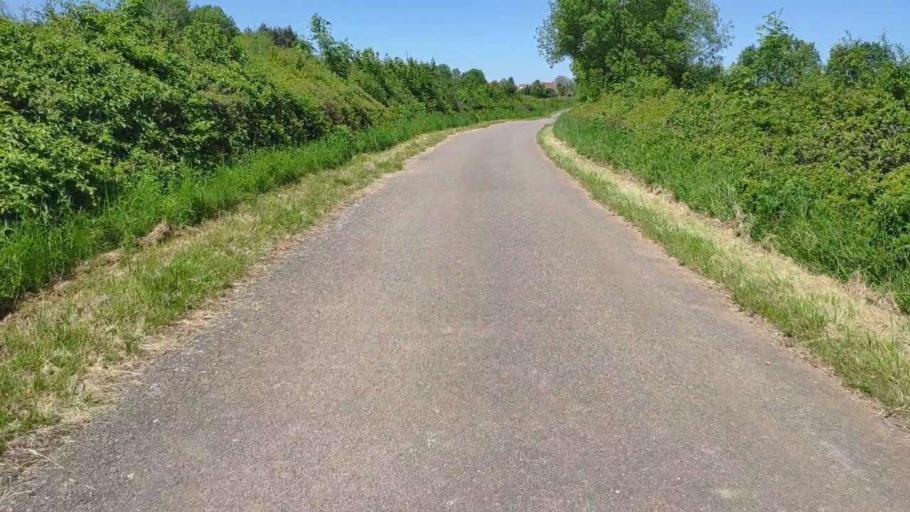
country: FR
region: Franche-Comte
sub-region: Departement du Jura
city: Perrigny
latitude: 46.7138
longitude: 5.6536
